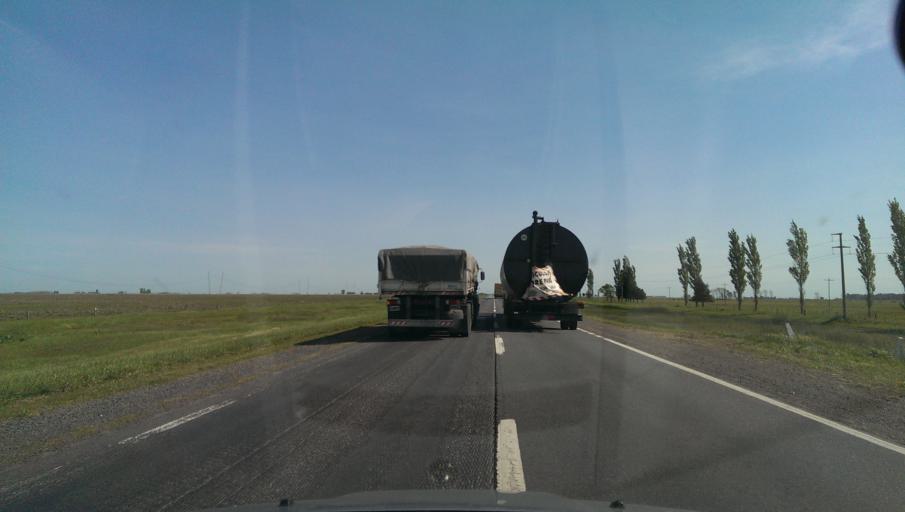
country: AR
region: Buenos Aires
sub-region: Partido de Azul
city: Azul
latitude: -36.6115
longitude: -59.6785
